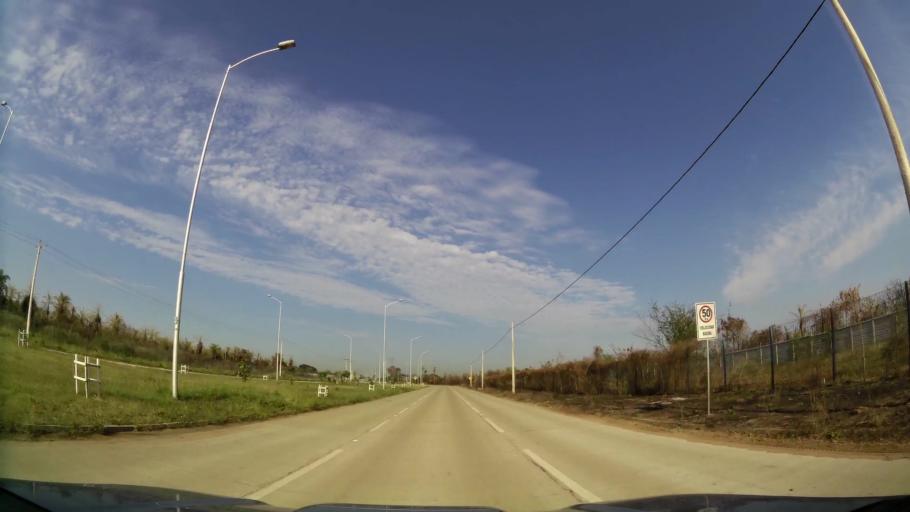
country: BO
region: Santa Cruz
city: Santa Cruz de la Sierra
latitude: -17.6938
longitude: -63.1198
